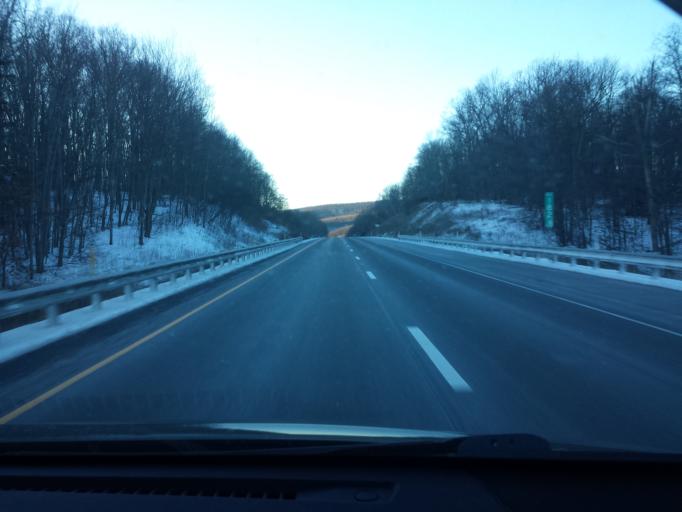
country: US
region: Pennsylvania
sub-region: Clinton County
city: Castanea
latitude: 41.0559
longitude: -77.3550
